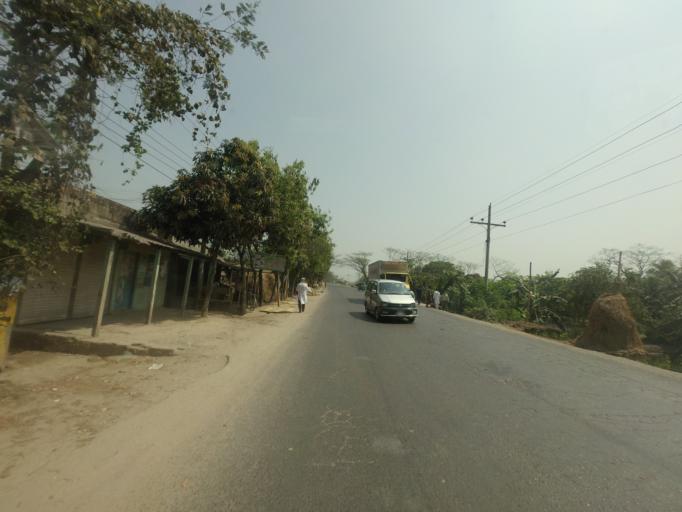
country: BD
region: Dhaka
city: Bhairab Bazar
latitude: 24.0542
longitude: 91.1490
